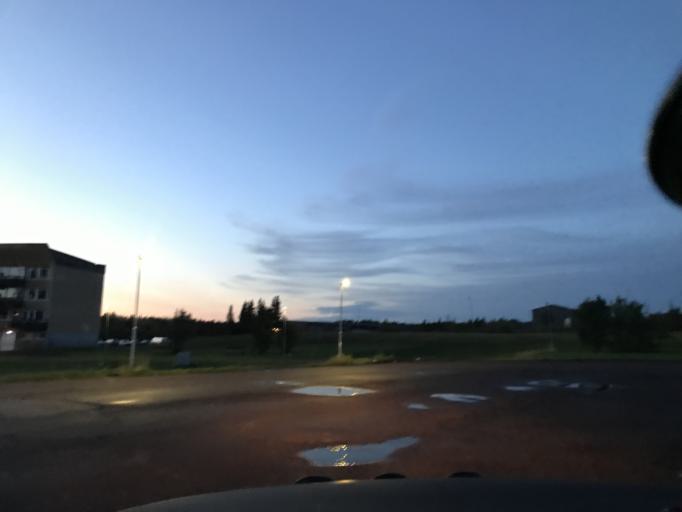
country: SE
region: Norrbotten
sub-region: Gallivare Kommun
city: Malmberget
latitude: 67.6486
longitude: 21.0577
